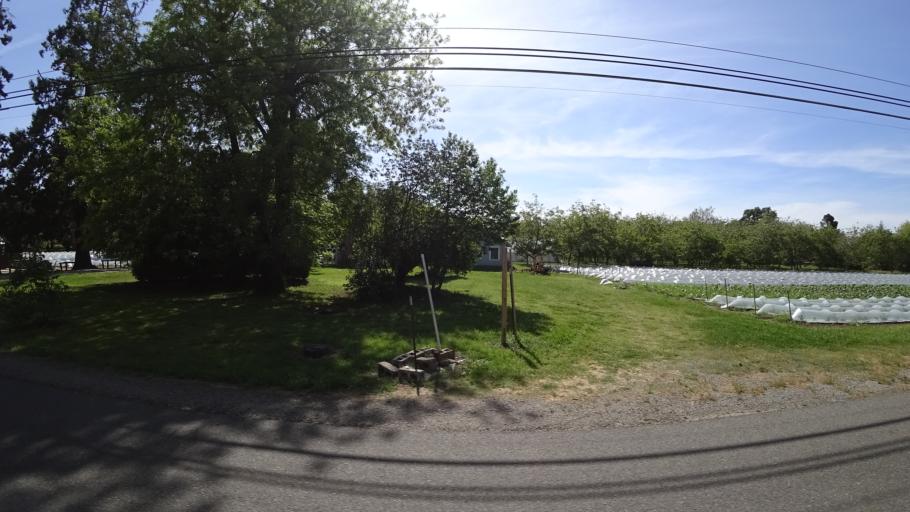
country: US
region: California
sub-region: Tehama County
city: Gerber
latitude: 40.1267
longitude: -122.1218
